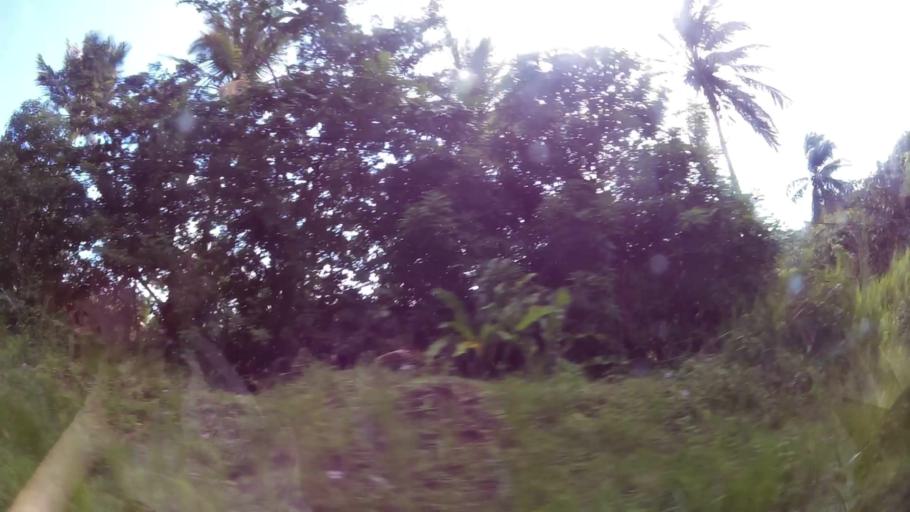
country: DM
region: Saint Andrew
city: Marigot
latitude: 15.4945
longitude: -61.2580
